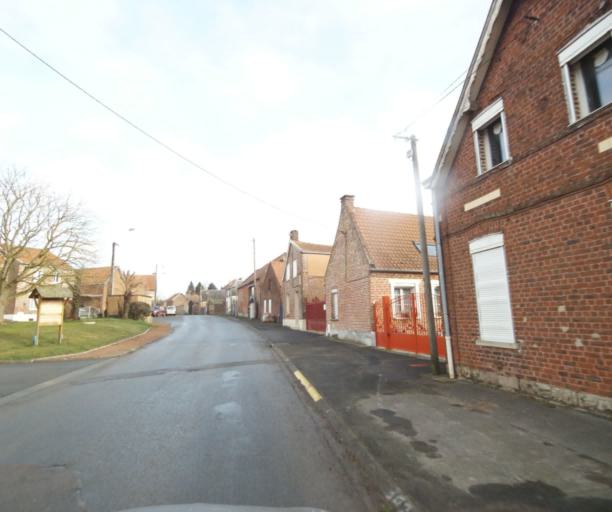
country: FR
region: Nord-Pas-de-Calais
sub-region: Departement du Nord
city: Vendegies-sur-Ecaillon
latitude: 50.2706
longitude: 3.4796
